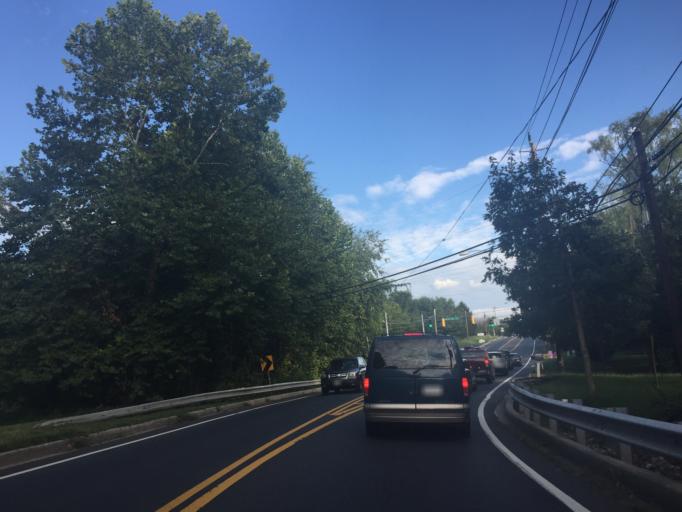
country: US
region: Maryland
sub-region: Montgomery County
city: Redland
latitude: 39.1346
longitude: -77.1234
